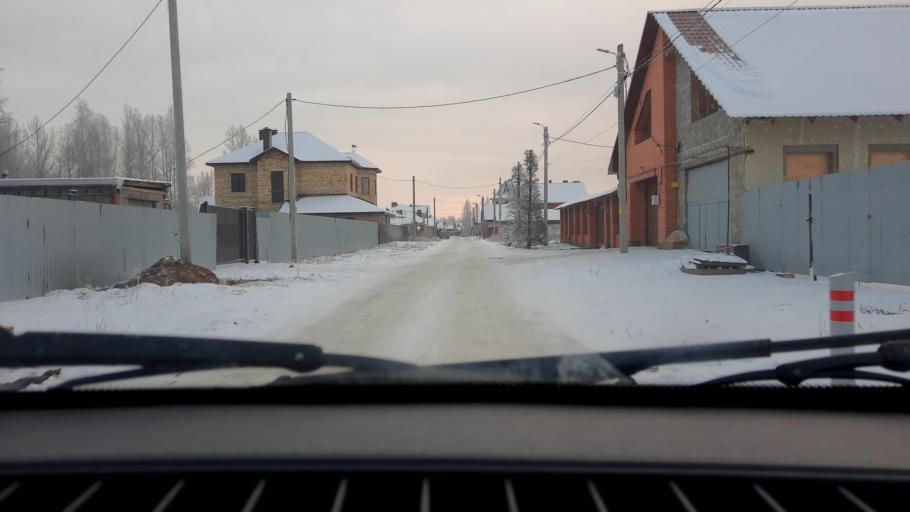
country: RU
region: Bashkortostan
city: Ufa
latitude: 54.6624
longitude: 55.9249
